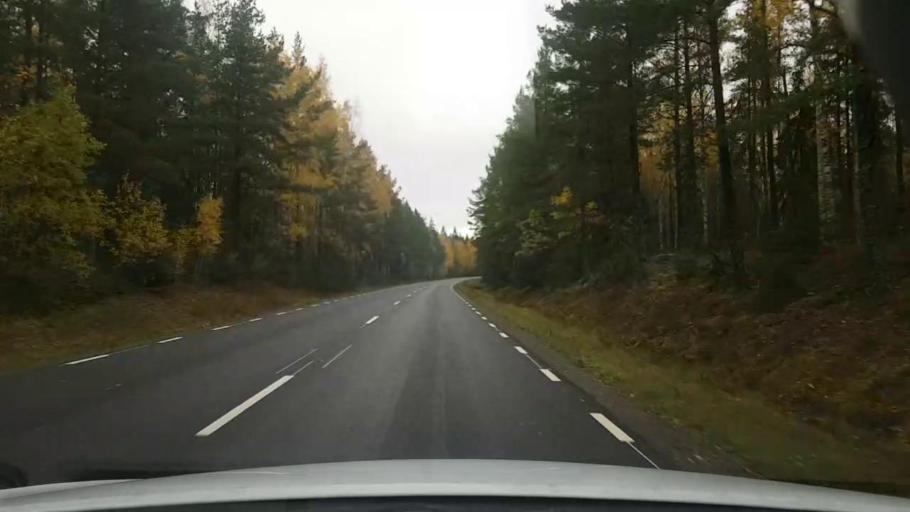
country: SE
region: OErebro
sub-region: Laxa Kommun
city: Laxa
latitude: 58.8004
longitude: 14.5424
